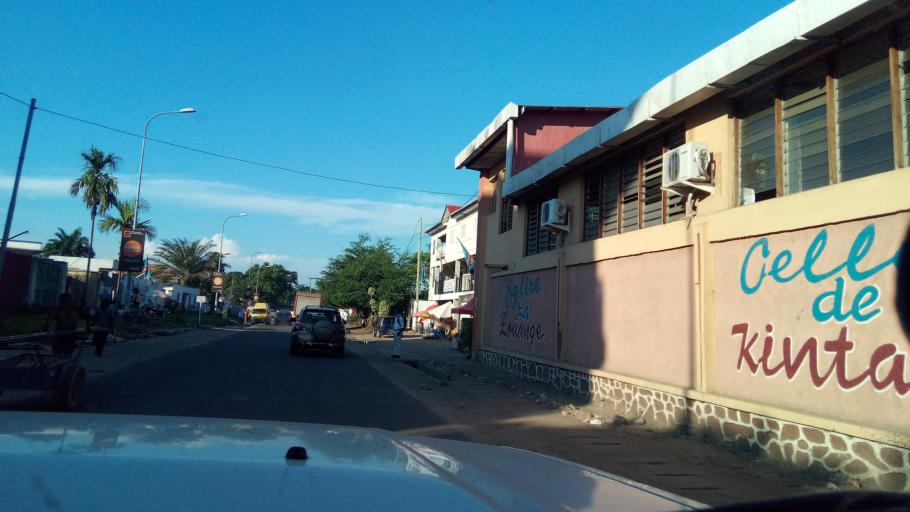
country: CD
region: Kinshasa
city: Kinshasa
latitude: -4.3507
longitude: 15.2643
